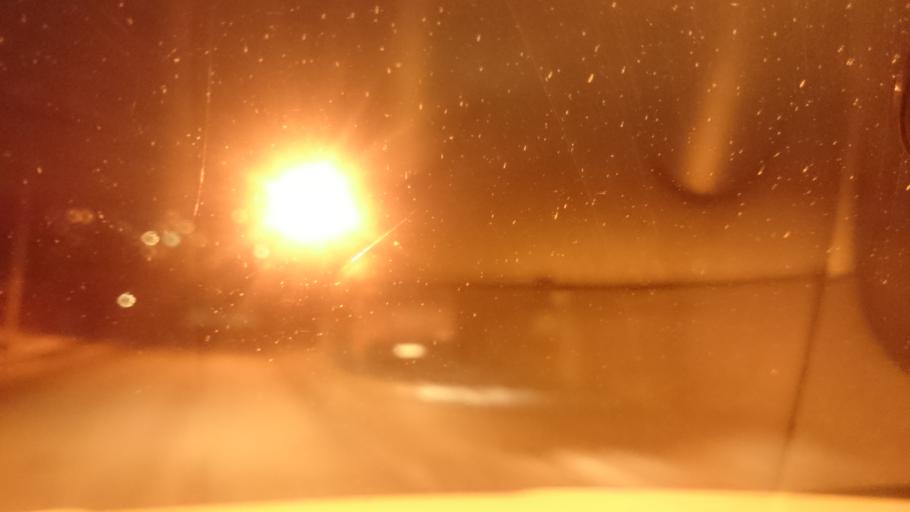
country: RU
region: Tula
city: Tula
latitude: 54.1852
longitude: 37.6341
